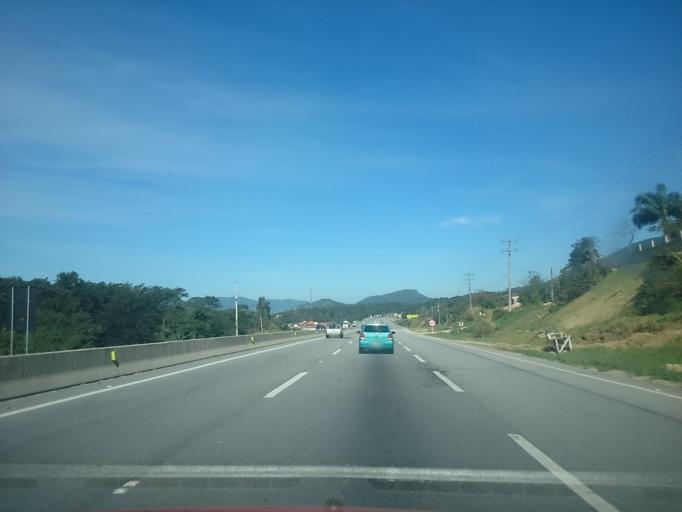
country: BR
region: Santa Catarina
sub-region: Palhoca
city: Palhoca
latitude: -27.7152
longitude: -48.6491
